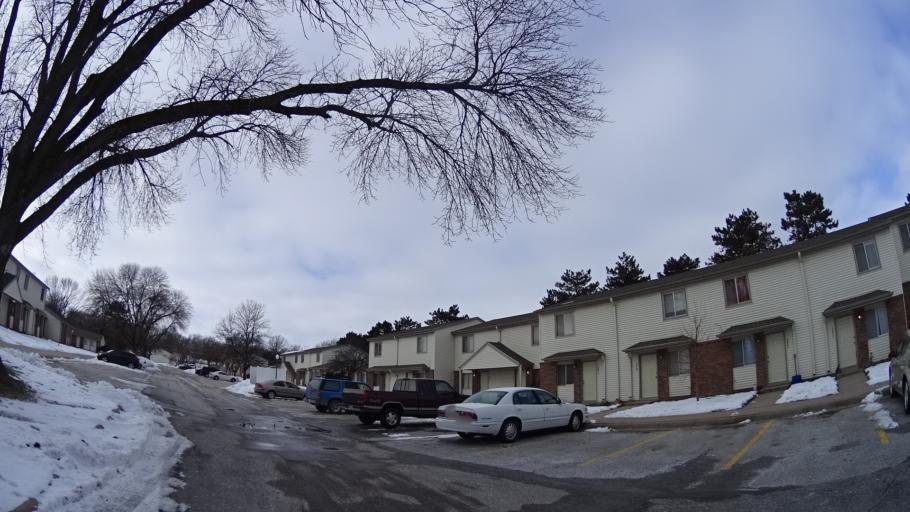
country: US
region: Nebraska
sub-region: Sarpy County
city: Offutt Air Force Base
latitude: 41.1191
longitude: -95.9540
